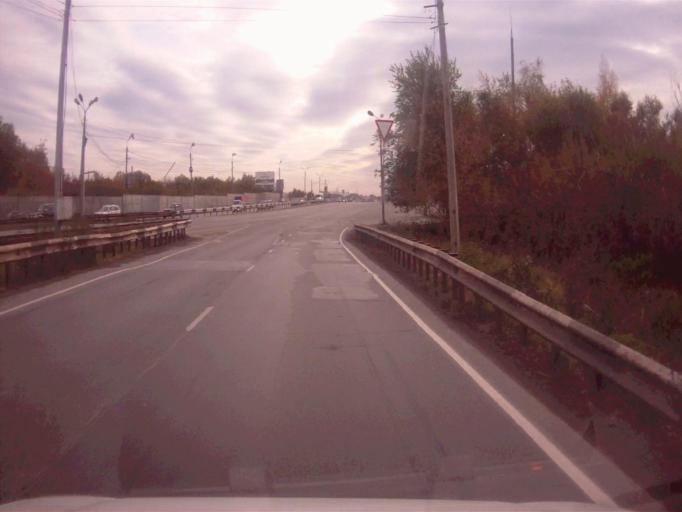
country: RU
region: Chelyabinsk
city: Novosineglazovskiy
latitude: 55.0778
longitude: 61.3883
